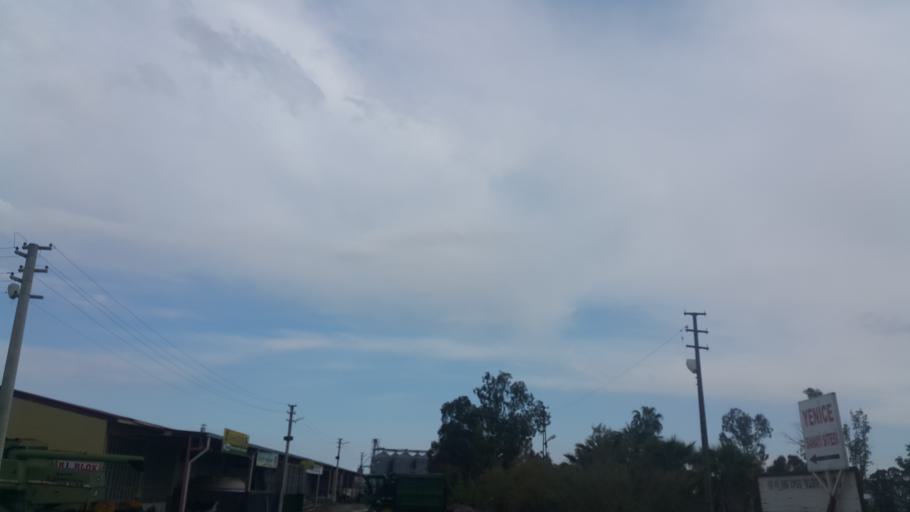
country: TR
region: Mersin
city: Yenice
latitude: 36.9743
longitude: 35.0611
